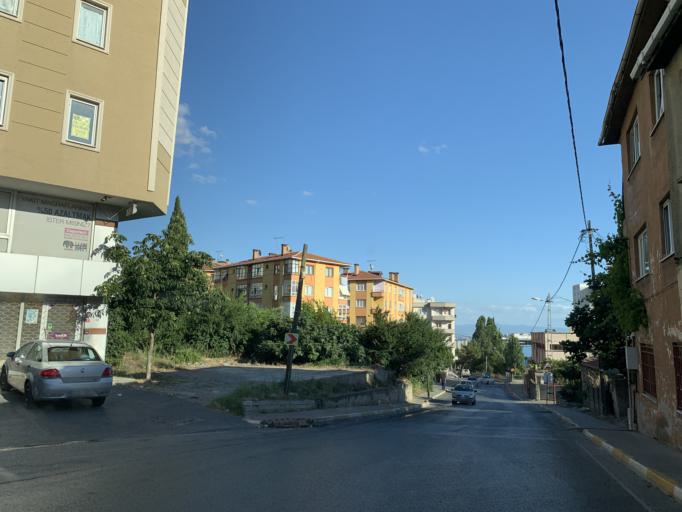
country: TR
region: Istanbul
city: Pendik
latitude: 40.9011
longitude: 29.2587
